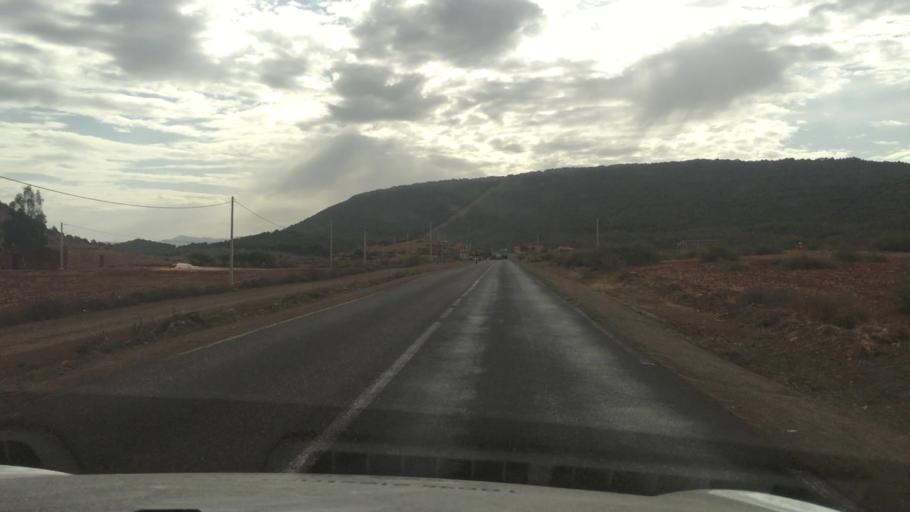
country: MA
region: Marrakech-Tensift-Al Haouz
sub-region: Al-Haouz
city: Touama
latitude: 31.5476
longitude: -7.5628
